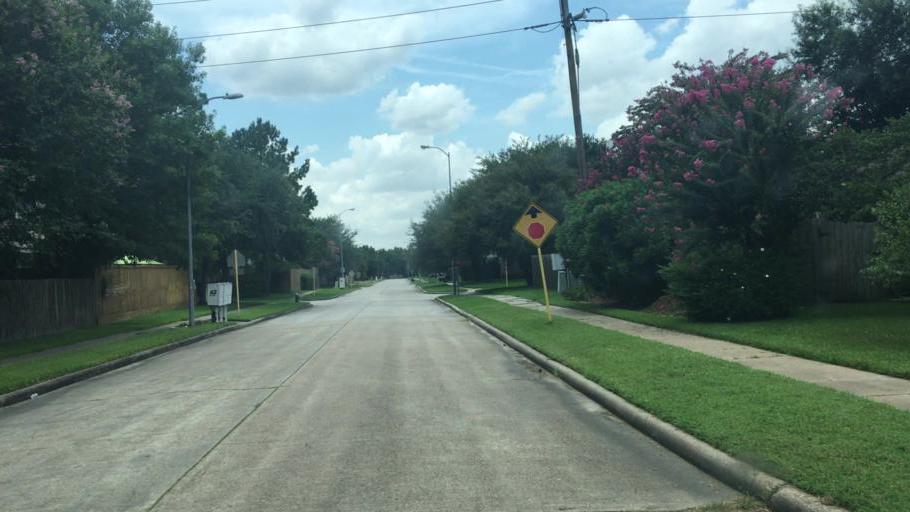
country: US
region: Texas
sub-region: Harris County
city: Atascocita
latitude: 29.9912
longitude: -95.1732
